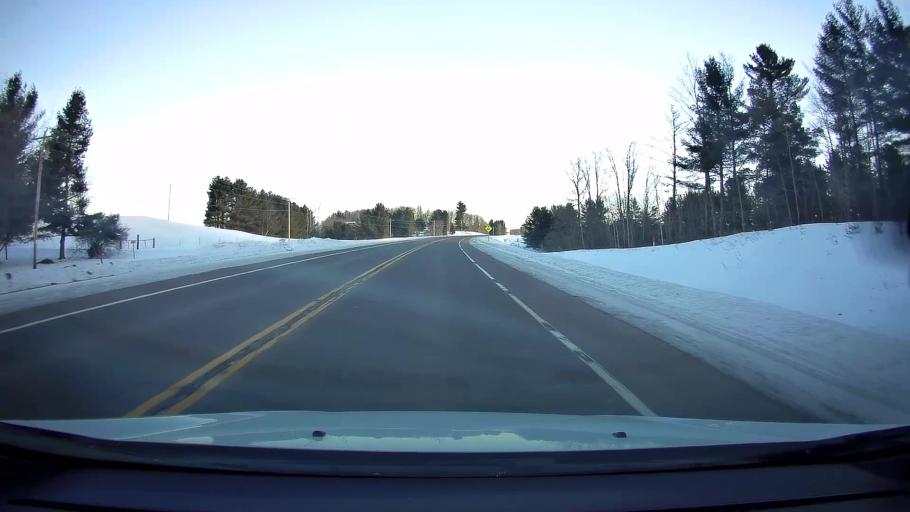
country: US
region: Wisconsin
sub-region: Barron County
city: Cumberland
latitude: 45.6004
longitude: -92.0171
